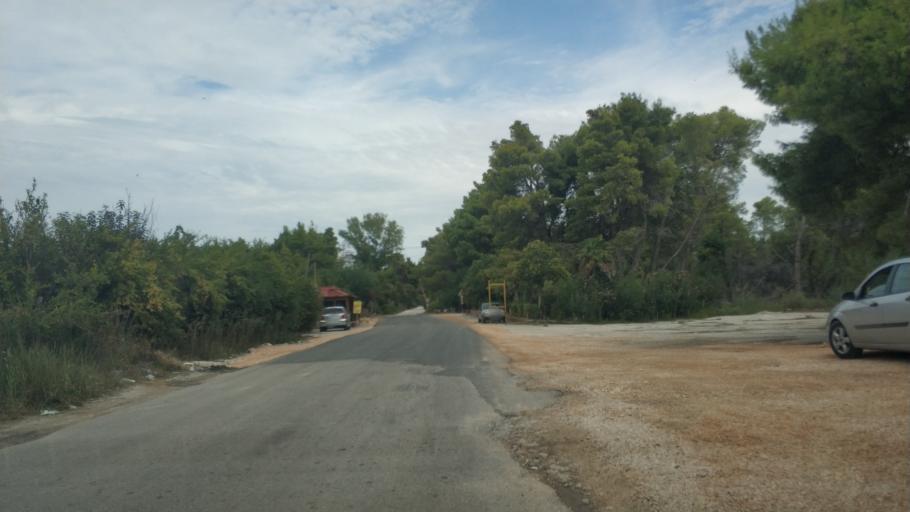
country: AL
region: Vlore
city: Vlore
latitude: 40.4777
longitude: 19.4522
